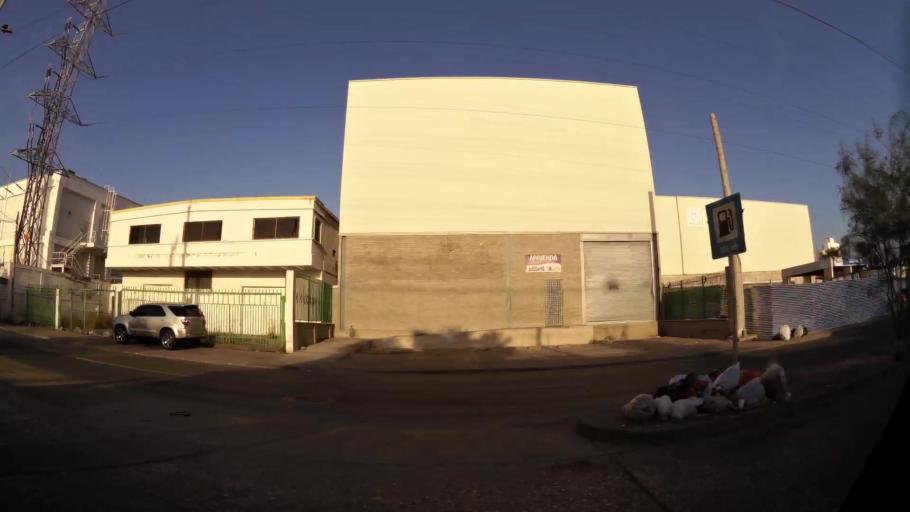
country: CO
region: Bolivar
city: Cartagena
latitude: 10.4089
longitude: -75.5217
